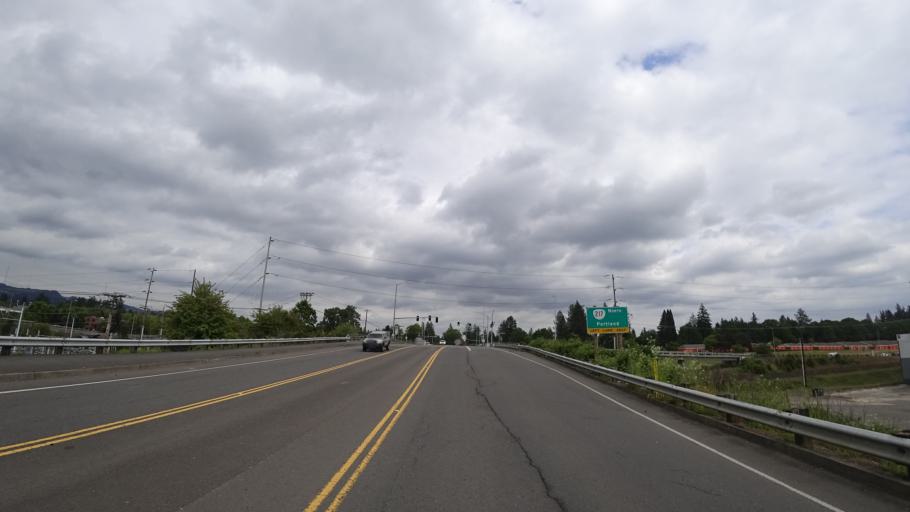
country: US
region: Oregon
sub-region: Washington County
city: Beaverton
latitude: 45.4693
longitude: -122.7878
